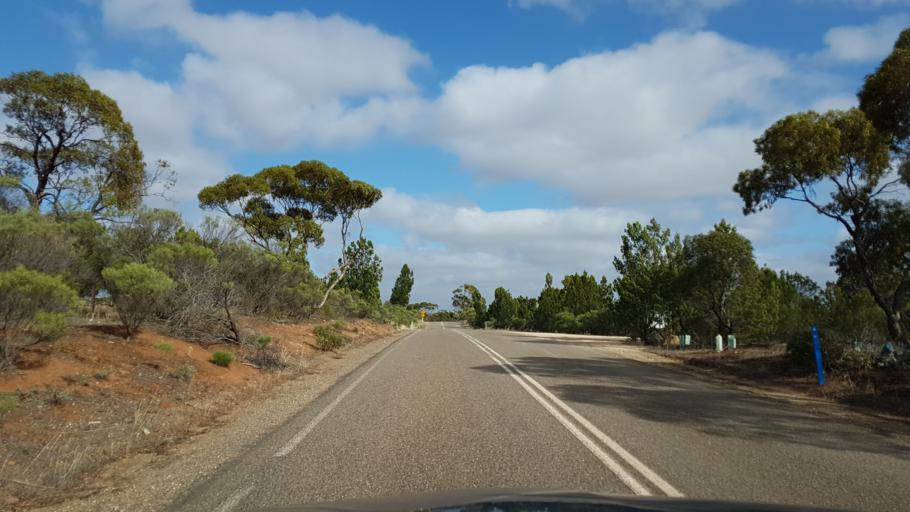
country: AU
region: South Australia
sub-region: Murray Bridge
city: Murray Bridge
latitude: -35.1133
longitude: 139.2266
